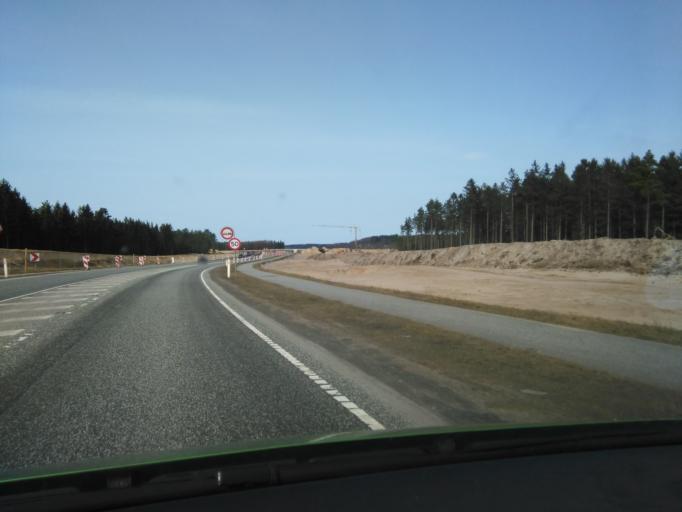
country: DK
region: Central Jutland
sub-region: Silkeborg Kommune
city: Svejbaek
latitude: 56.1638
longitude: 9.6081
